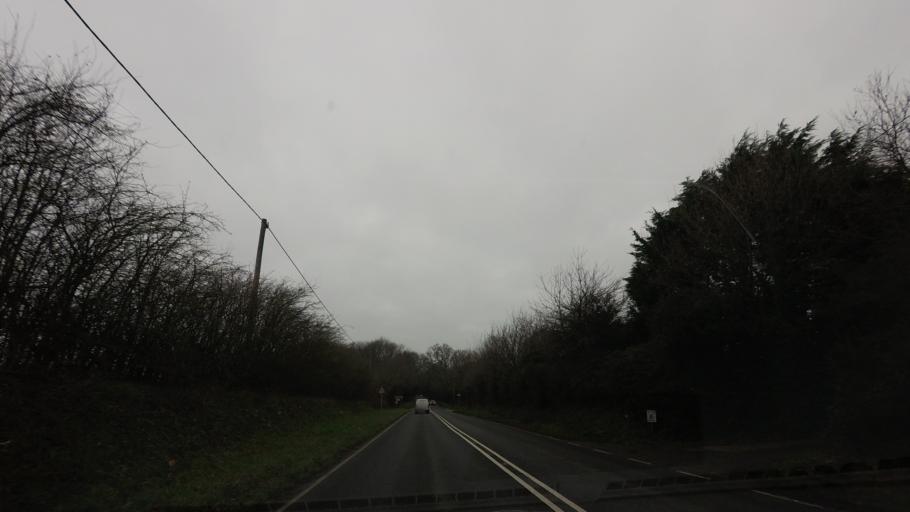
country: GB
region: England
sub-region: East Sussex
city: Battle
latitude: 50.9412
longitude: 0.5136
